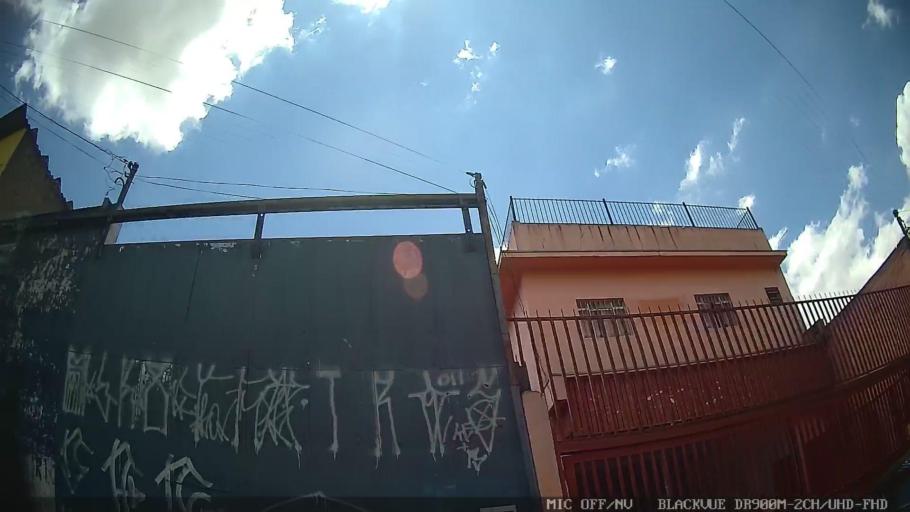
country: BR
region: Sao Paulo
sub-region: Diadema
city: Diadema
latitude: -23.6516
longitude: -46.6543
